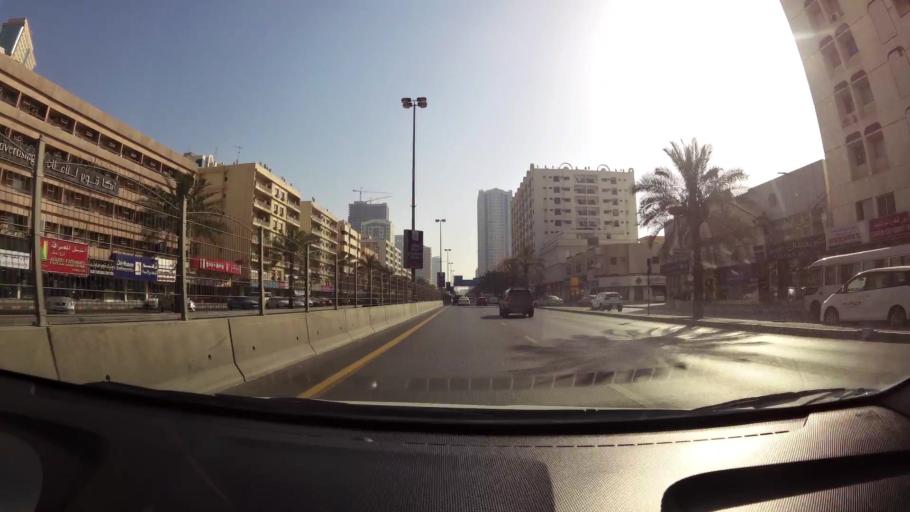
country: AE
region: Ash Shariqah
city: Sharjah
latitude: 25.3195
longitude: 55.3870
